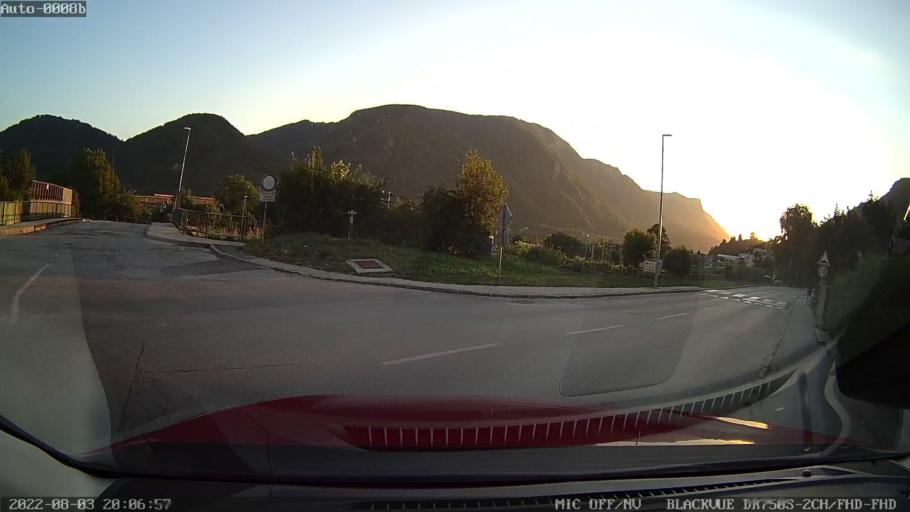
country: SI
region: Jesenice
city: Slovenski Javornik
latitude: 46.4257
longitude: 14.0980
